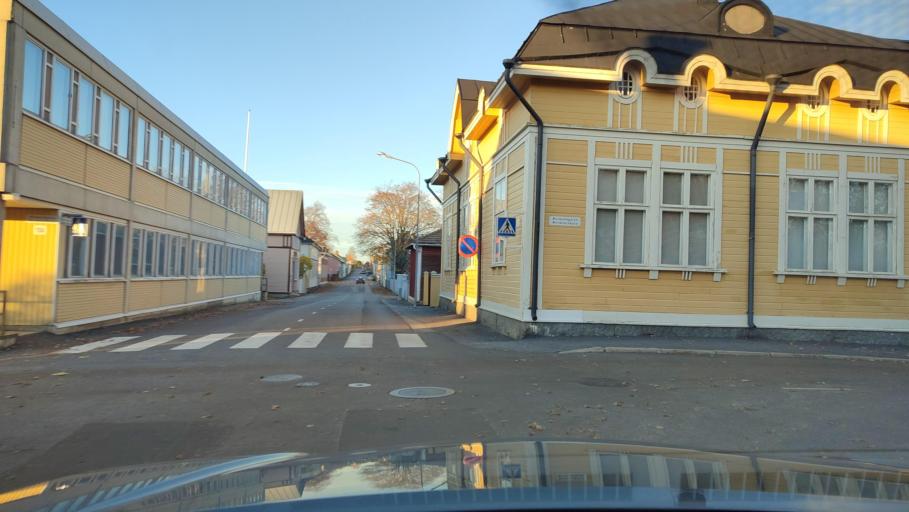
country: FI
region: Ostrobothnia
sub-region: Sydosterbotten
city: Kristinestad
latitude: 62.2729
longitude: 21.3760
